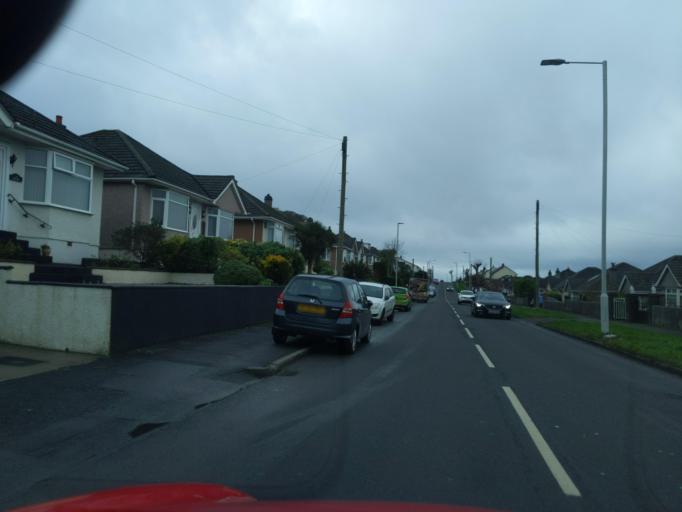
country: GB
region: England
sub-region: Plymouth
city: Plymstock
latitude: 50.3612
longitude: -4.0699
